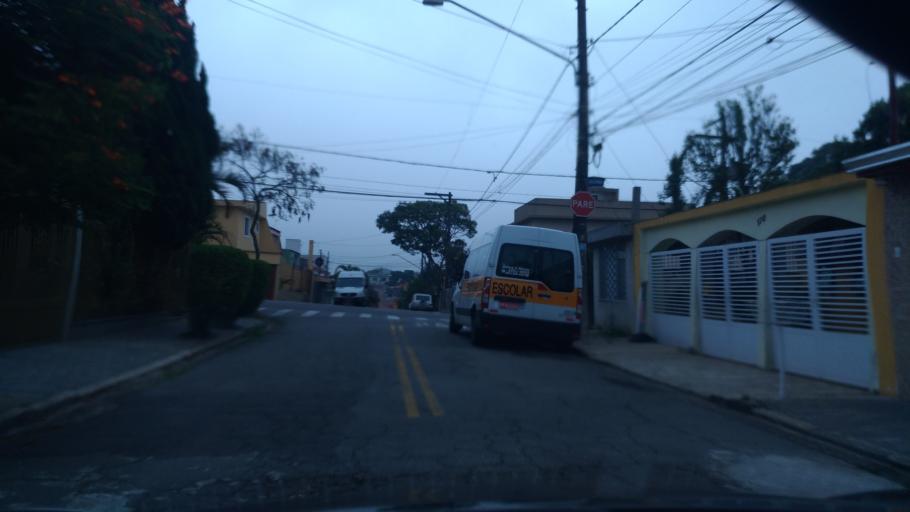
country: BR
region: Sao Paulo
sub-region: Sao Bernardo Do Campo
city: Sao Bernardo do Campo
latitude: -23.7194
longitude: -46.5695
